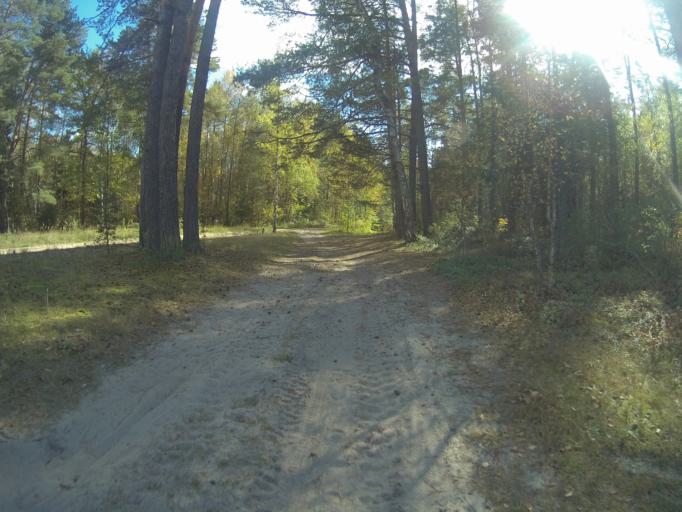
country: RU
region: Vladimir
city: Kommunar
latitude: 56.0380
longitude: 40.4637
